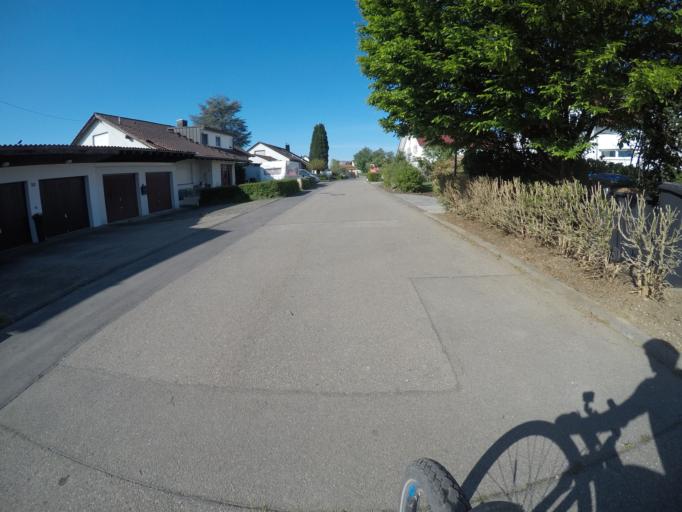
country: DE
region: Baden-Wuerttemberg
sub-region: Regierungsbezirk Stuttgart
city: Altenriet
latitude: 48.5989
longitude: 9.2004
